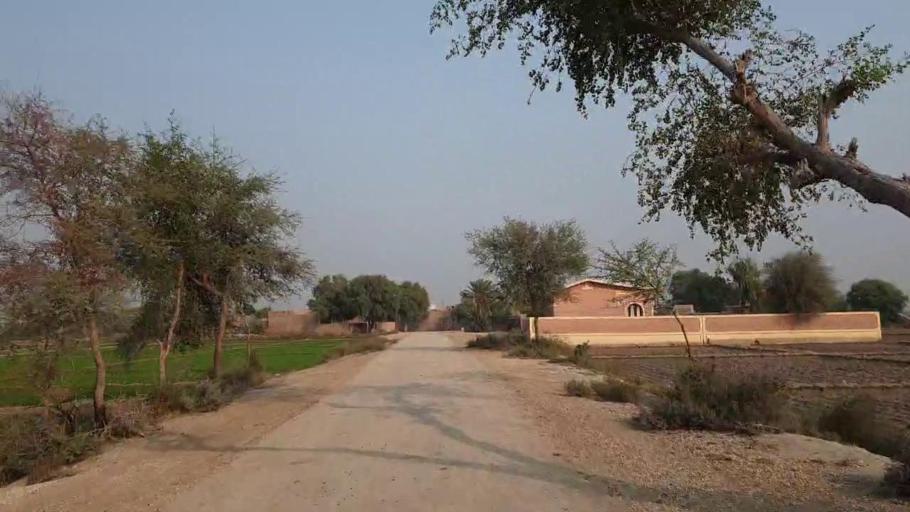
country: PK
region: Sindh
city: Bhan
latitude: 26.4893
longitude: 67.7281
